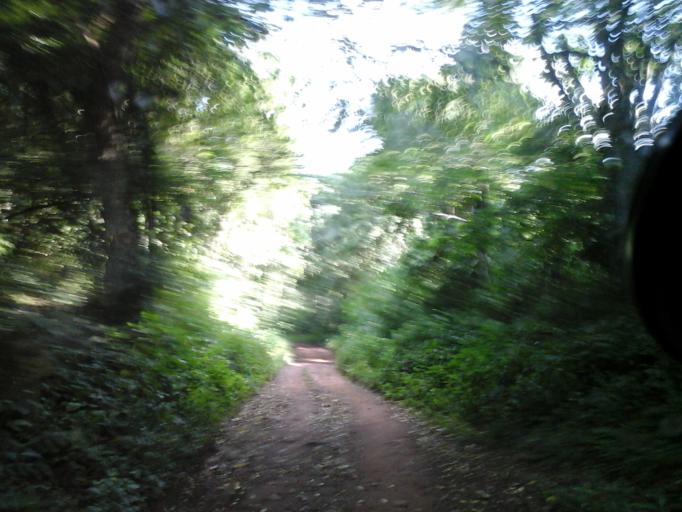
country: CO
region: Cesar
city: San Diego
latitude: 10.2609
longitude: -73.1085
